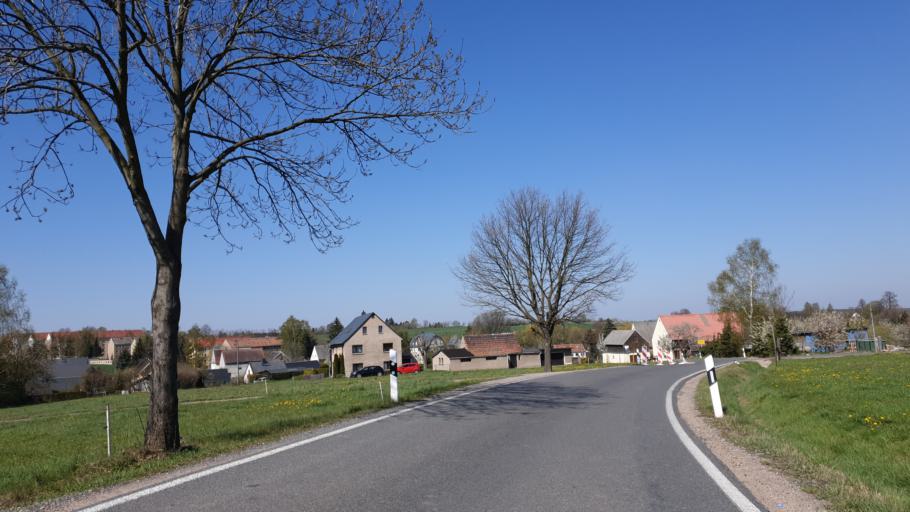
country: DE
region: Saxony
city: Taura
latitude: 50.9270
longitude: 12.8293
